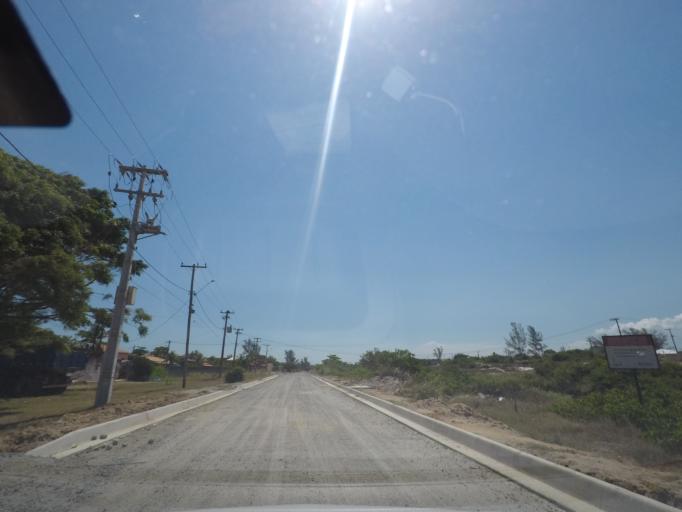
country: BR
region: Rio de Janeiro
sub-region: Marica
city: Marica
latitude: -22.9695
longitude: -42.9039
